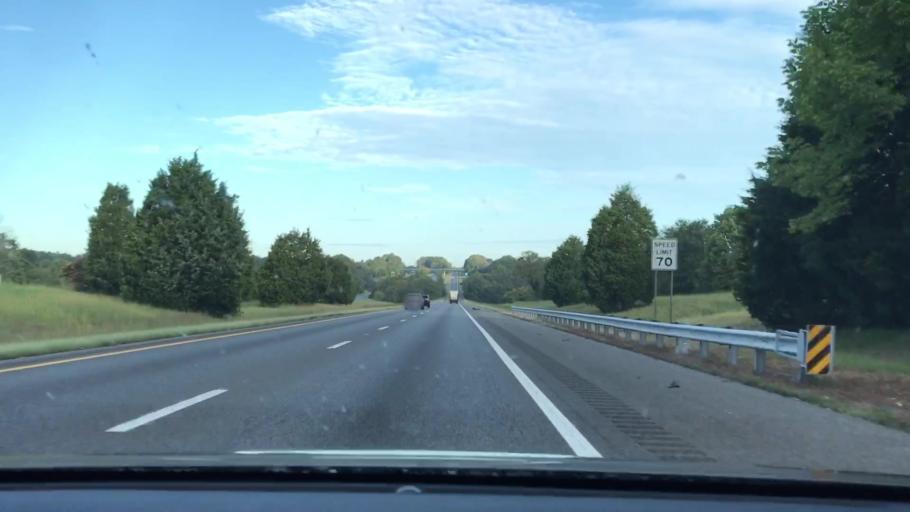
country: US
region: Tennessee
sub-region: Montgomery County
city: Clarksville
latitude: 36.6094
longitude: -87.2905
